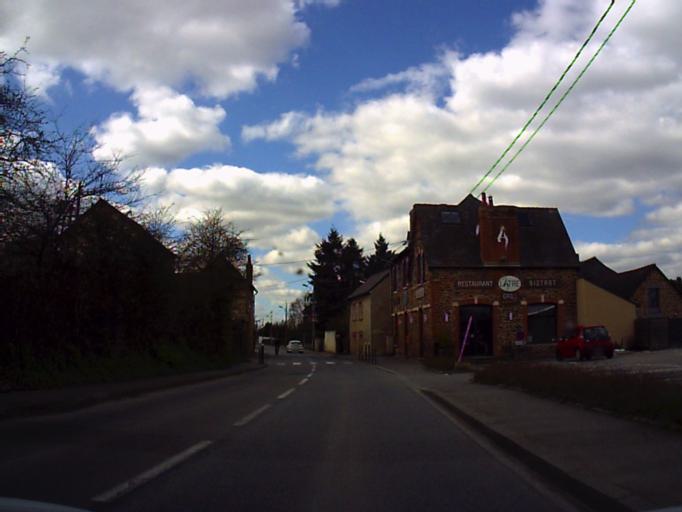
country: FR
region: Brittany
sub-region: Departement d'Ille-et-Vilaine
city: Saint-Jacques-de-la-Lande
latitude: 48.1010
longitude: -1.7204
